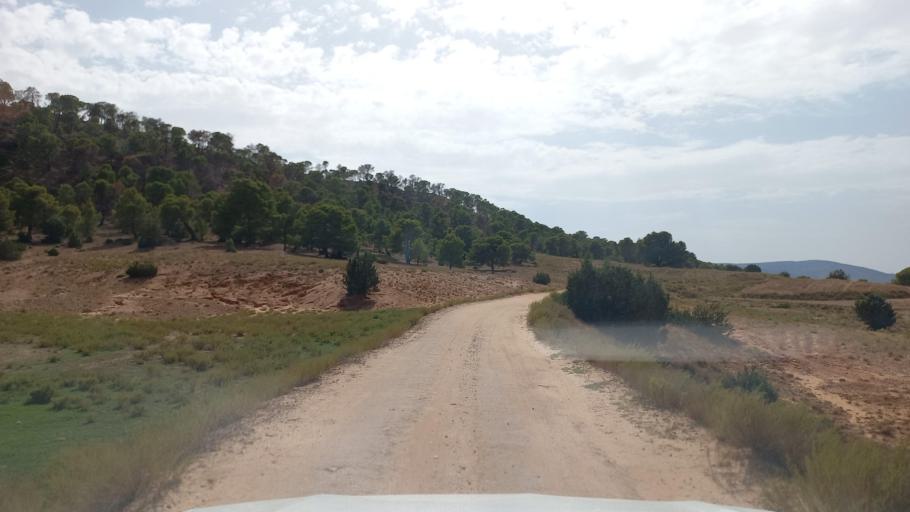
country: TN
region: Al Qasrayn
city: Kasserine
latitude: 35.3523
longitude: 8.8853
